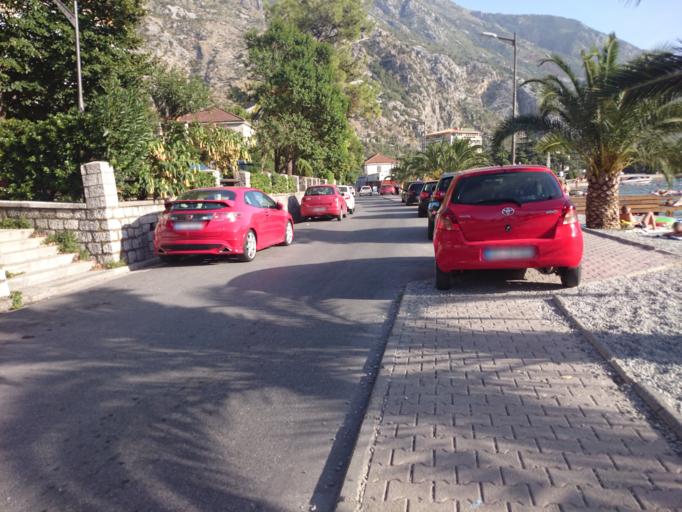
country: ME
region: Kotor
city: Kotor
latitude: 42.4300
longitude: 18.7678
